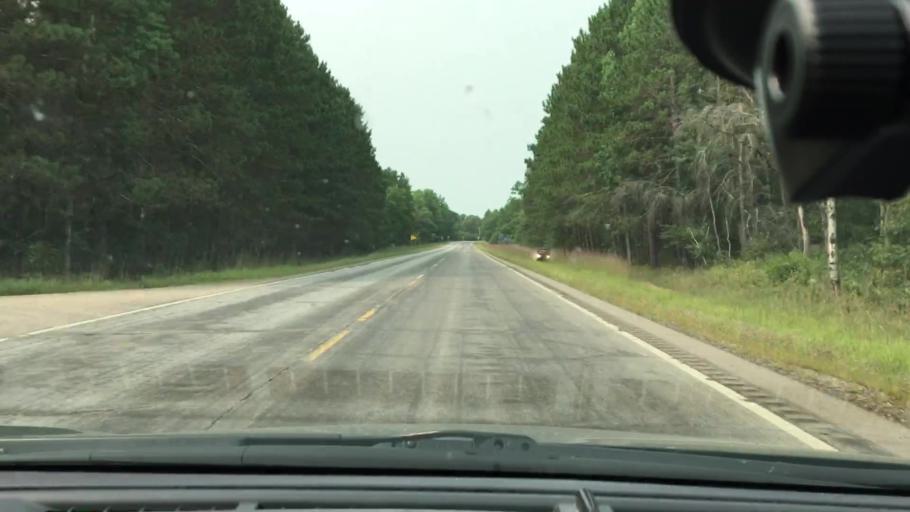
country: US
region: Minnesota
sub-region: Crow Wing County
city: Cross Lake
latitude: 46.7392
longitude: -93.9635
